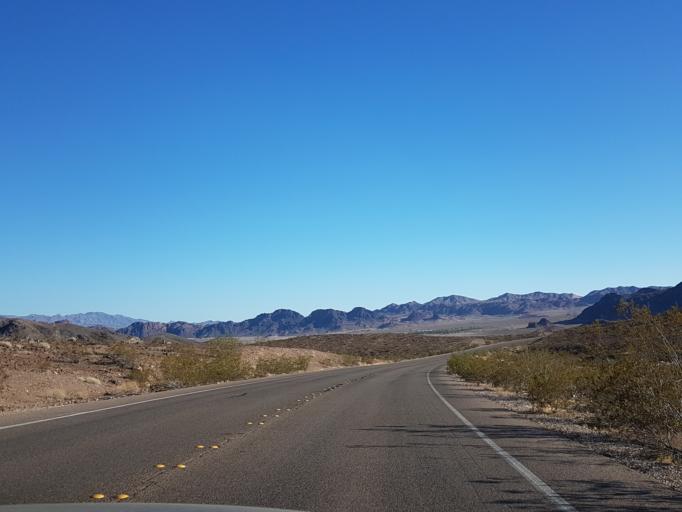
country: US
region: Nevada
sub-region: Clark County
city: Boulder City
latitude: 36.0747
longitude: -114.8208
